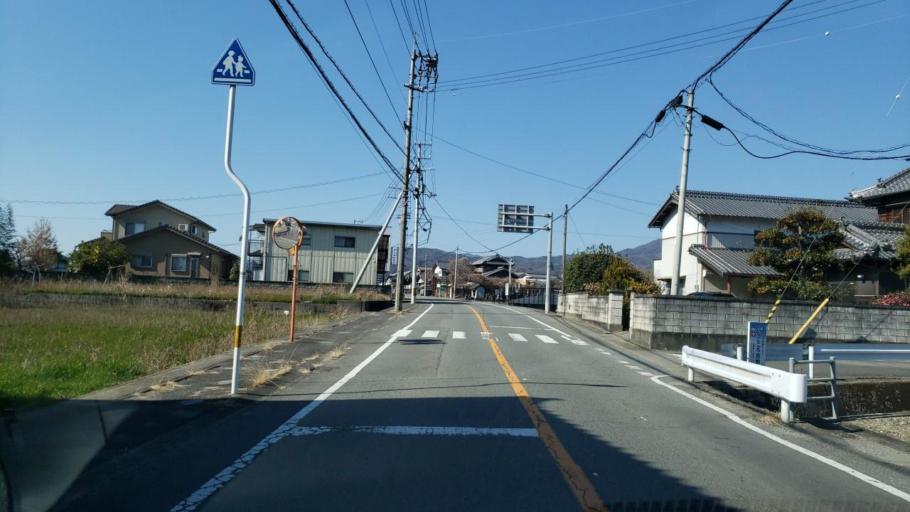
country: JP
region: Tokushima
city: Kamojimacho-jogejima
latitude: 34.0971
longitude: 134.3411
